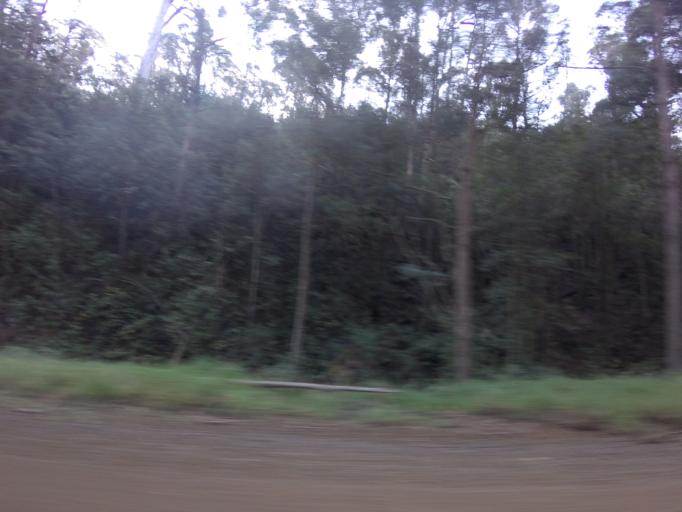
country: AU
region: Tasmania
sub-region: Sorell
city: Sorell
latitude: -42.4853
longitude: 147.4385
